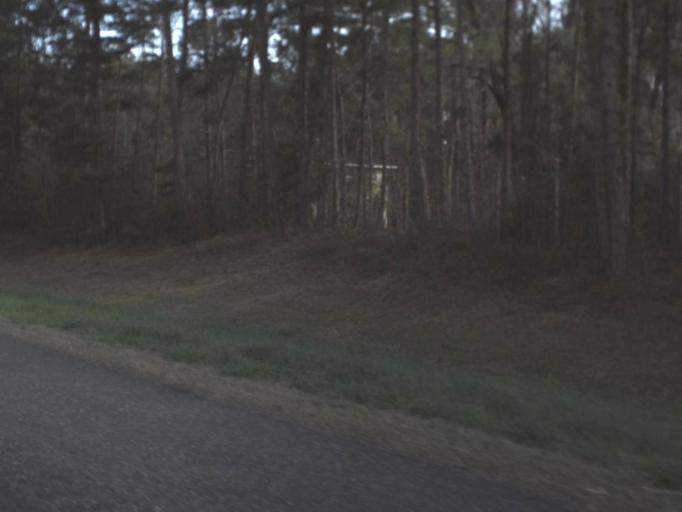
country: US
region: Florida
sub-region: Leon County
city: Tallahassee
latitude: 30.4781
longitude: -84.1303
